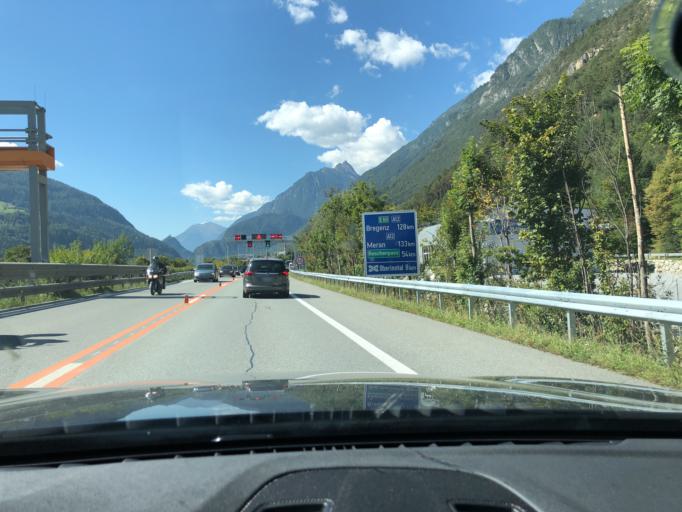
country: AT
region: Tyrol
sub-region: Politischer Bezirk Imst
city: Imsterberg
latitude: 47.2118
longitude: 10.6897
